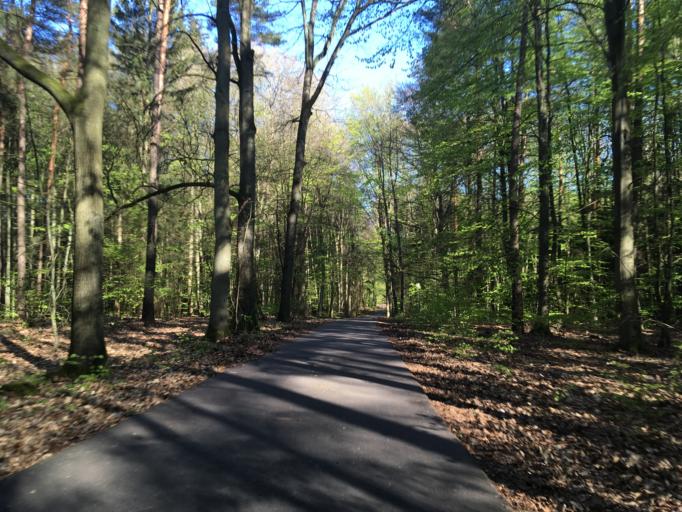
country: DE
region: Brandenburg
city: Wandlitz
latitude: 52.7331
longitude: 13.5042
